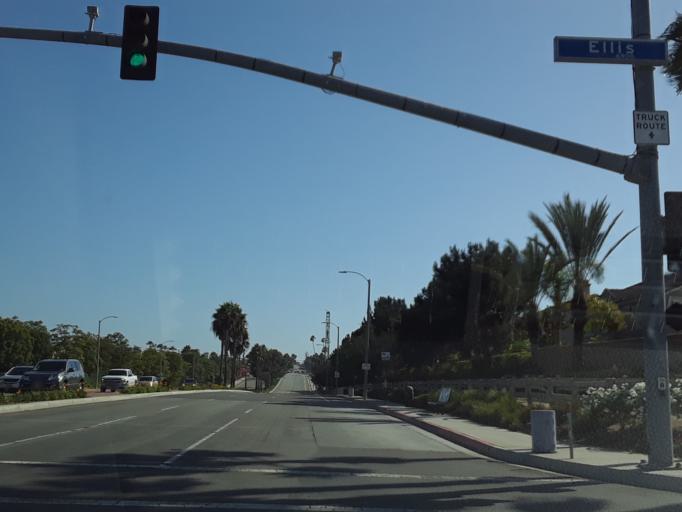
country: US
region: California
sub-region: Orange County
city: Huntington Beach
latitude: 33.6937
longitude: -118.0064
